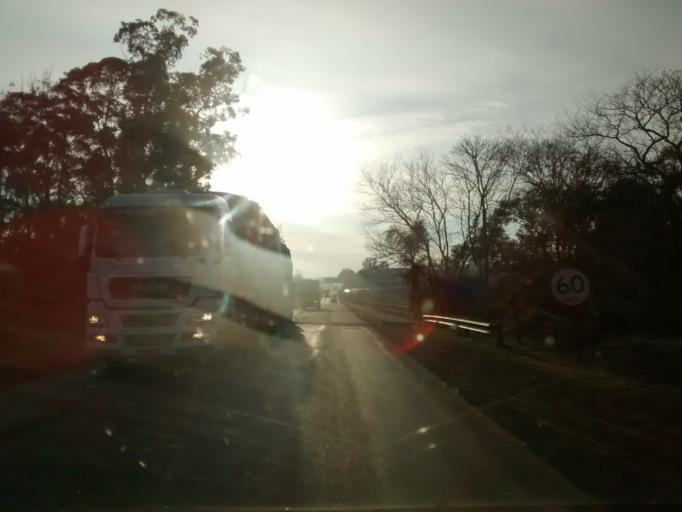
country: BR
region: Parana
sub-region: Francisco Beltrao
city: Francisco Beltrao
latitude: -26.1525
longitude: -53.0210
